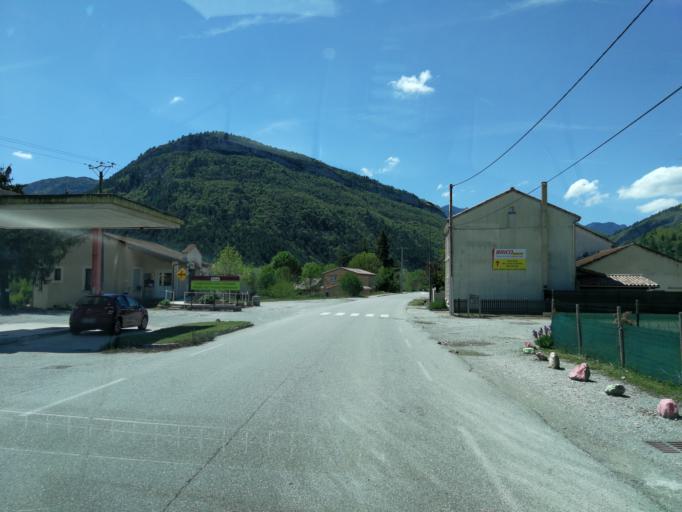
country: FR
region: Rhone-Alpes
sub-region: Departement de la Drome
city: Die
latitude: 44.7033
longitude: 5.2576
